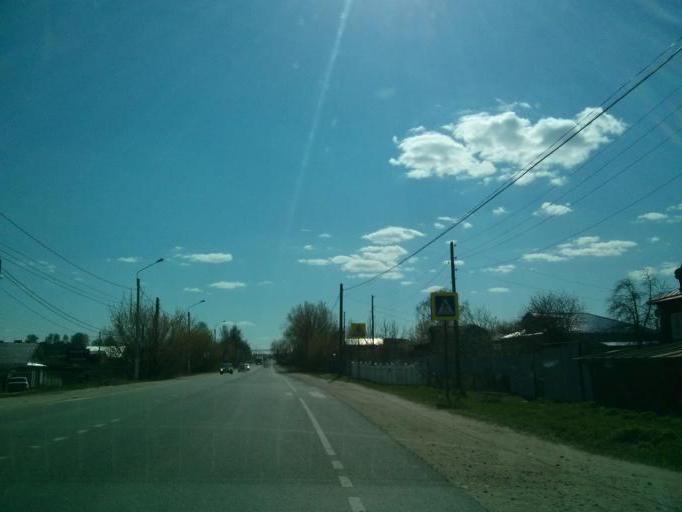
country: RU
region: Nizjnij Novgorod
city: Taremskoye
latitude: 55.9291
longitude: 43.0400
